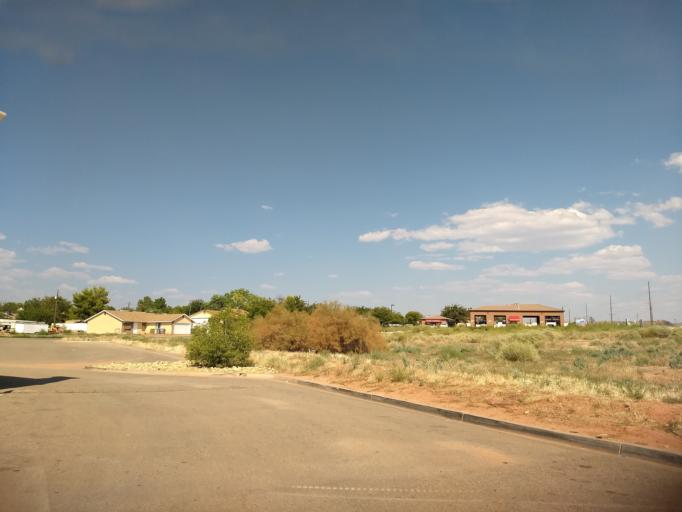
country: US
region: Utah
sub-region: Washington County
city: Washington
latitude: 37.1306
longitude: -113.4997
